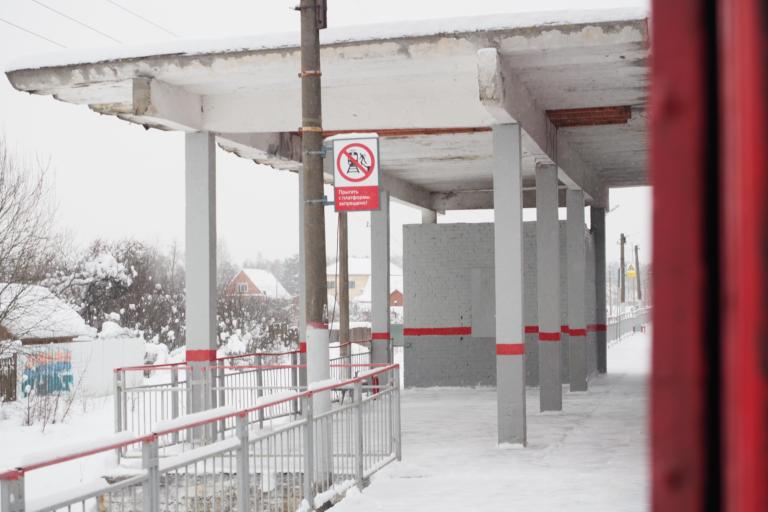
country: RU
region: Moskovskaya
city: Fosforitnyy
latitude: 55.3392
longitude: 38.8893
